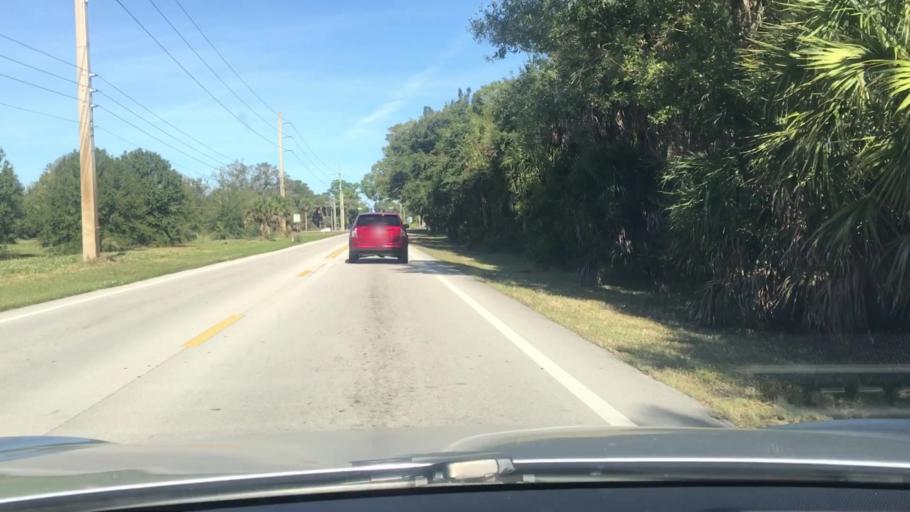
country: US
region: Florida
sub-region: Indian River County
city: Winter Beach
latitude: 27.7463
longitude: -80.4619
